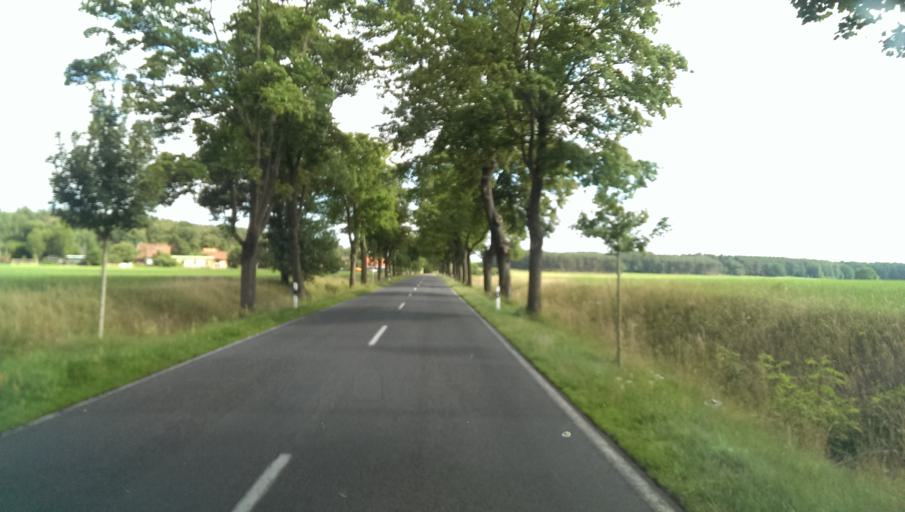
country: DE
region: Saxony-Anhalt
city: Radis
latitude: 51.6943
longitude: 12.5176
